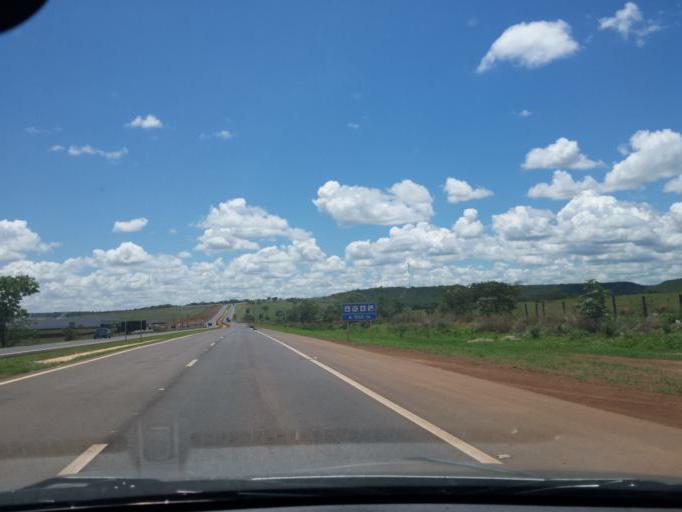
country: BR
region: Goias
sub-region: Cristalina
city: Cristalina
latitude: -16.6179
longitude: -47.7536
